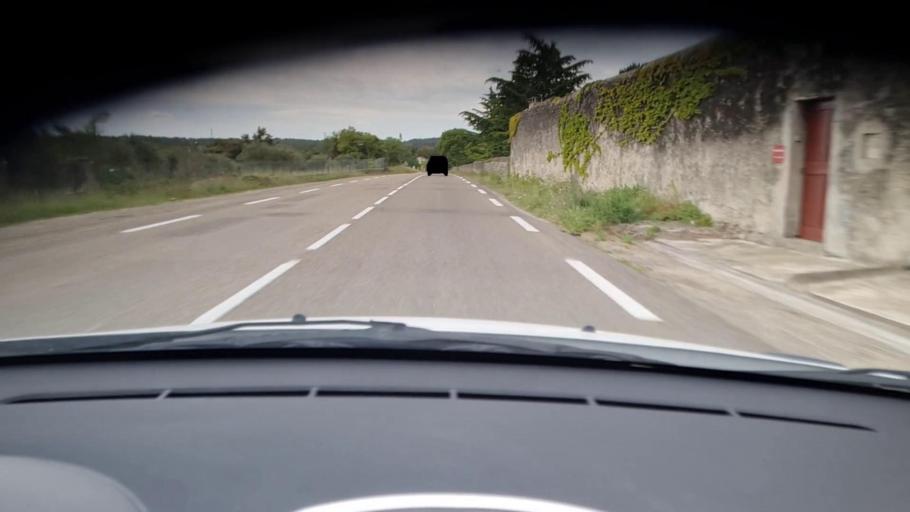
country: FR
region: Languedoc-Roussillon
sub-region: Departement du Gard
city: Uzes
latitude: 43.9956
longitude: 4.4131
